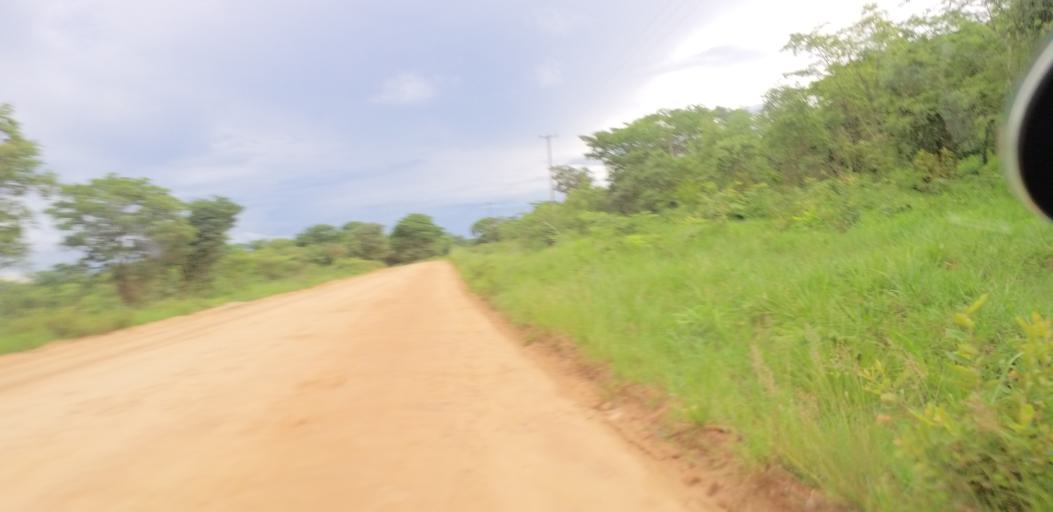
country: ZM
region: Lusaka
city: Chongwe
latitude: -15.1794
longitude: 28.4535
